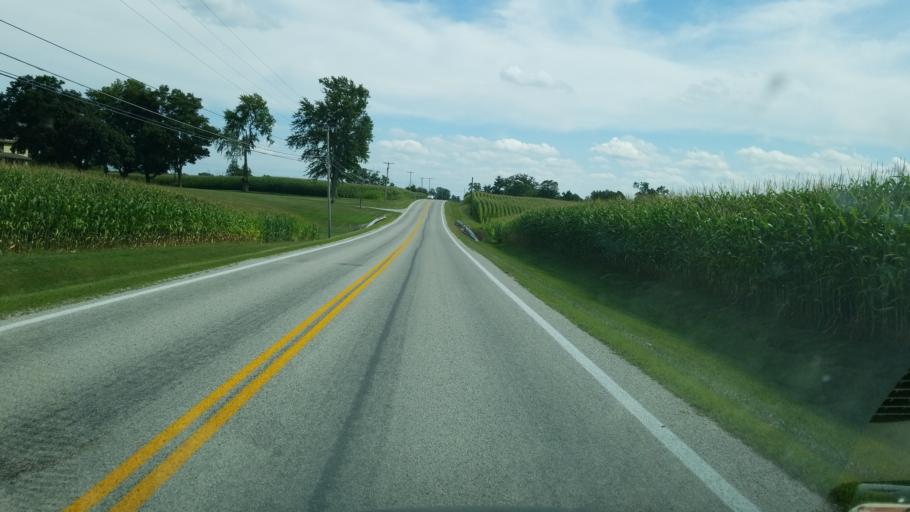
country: US
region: Ohio
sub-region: Marion County
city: Marion
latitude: 40.5018
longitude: -83.0932
